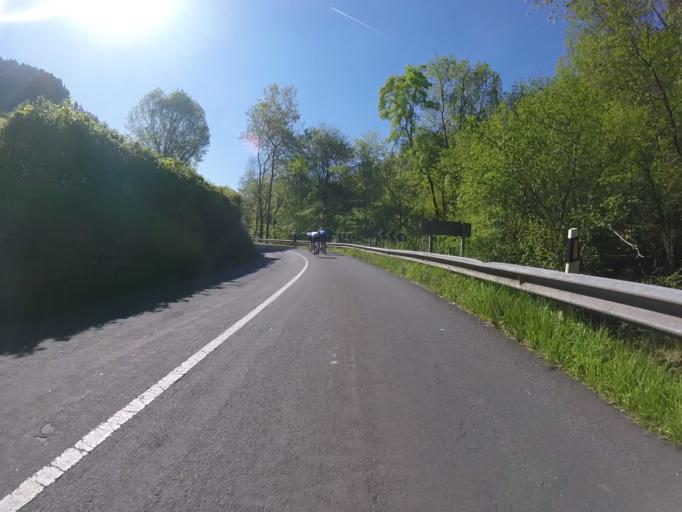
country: ES
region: Basque Country
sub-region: Provincia de Guipuzcoa
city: Errezil
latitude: 43.1734
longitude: -2.2002
